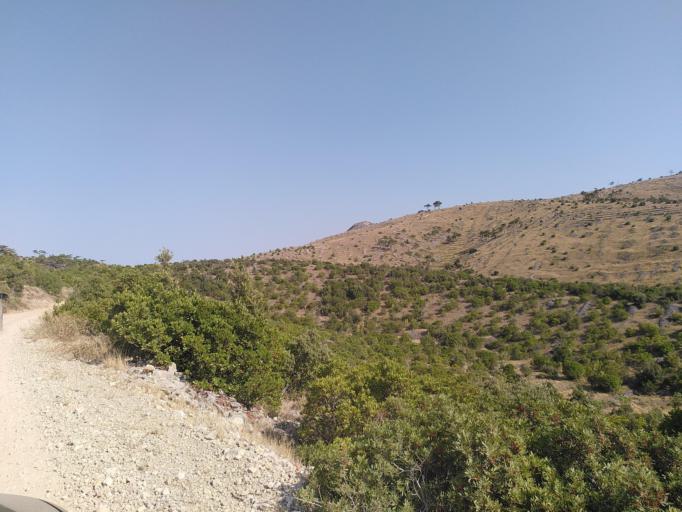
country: HR
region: Splitsko-Dalmatinska
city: Stari Grad
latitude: 43.1536
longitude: 16.5828
